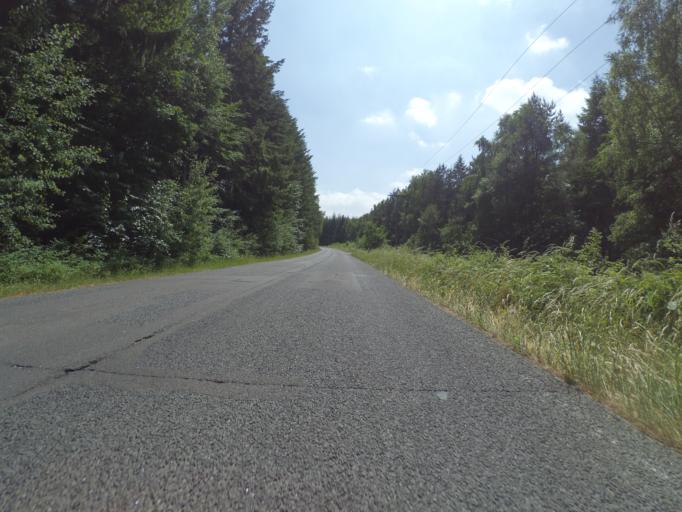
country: DE
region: Mecklenburg-Vorpommern
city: Plau am See
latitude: 53.3977
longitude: 12.3205
